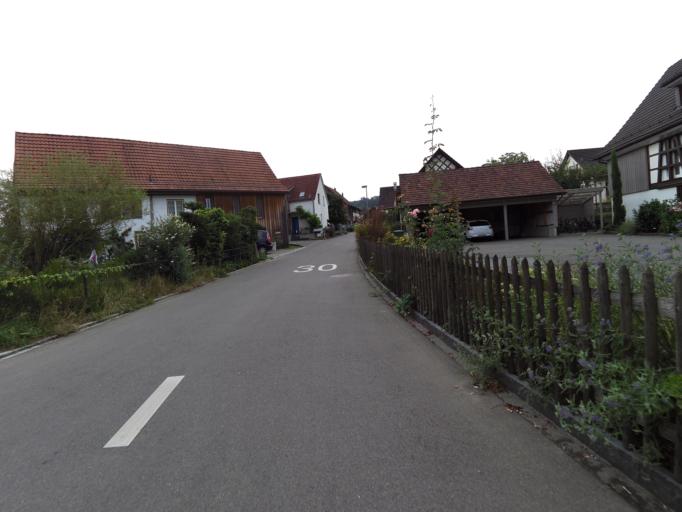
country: CH
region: Thurgau
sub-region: Kreuzlingen District
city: Tagerwilen
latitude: 47.6538
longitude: 9.1366
